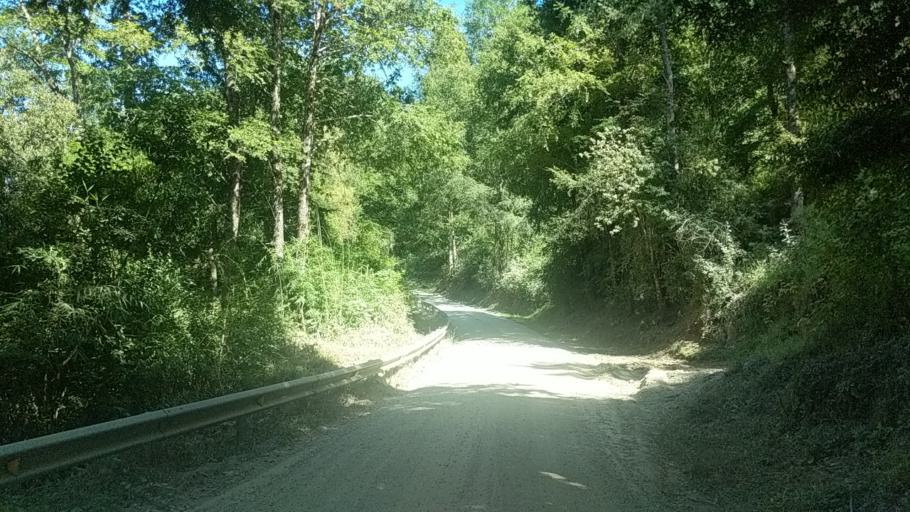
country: CL
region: Araucania
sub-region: Provincia de Cautin
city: Pucon
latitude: -39.0637
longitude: -71.7133
